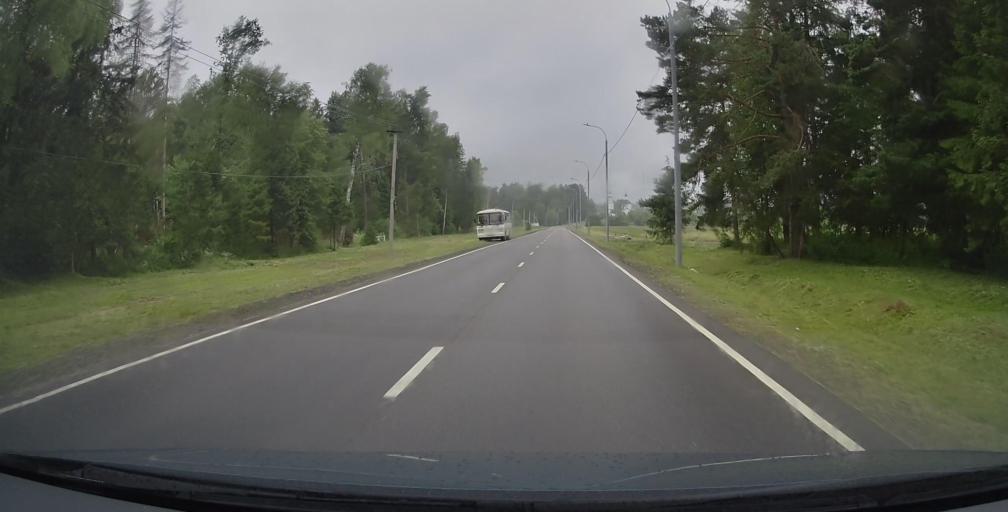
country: RU
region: Moskovskaya
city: Selyatino
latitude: 55.4245
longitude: 36.9671
